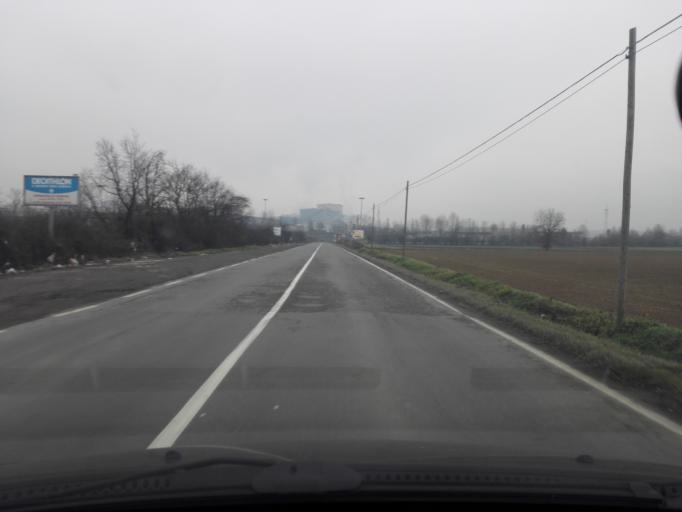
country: IT
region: Piedmont
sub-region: Provincia di Alessandria
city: Pasturana
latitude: 44.7816
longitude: 8.7518
